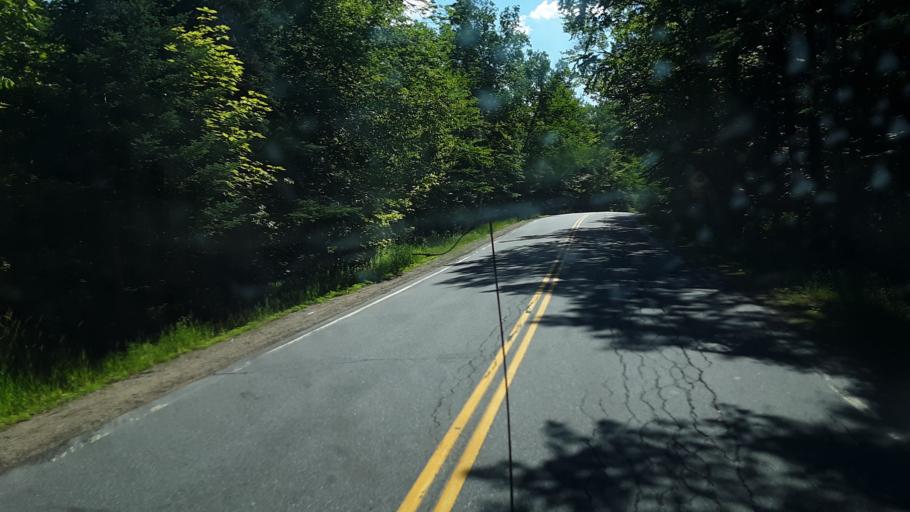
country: US
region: New Hampshire
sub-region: Grafton County
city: North Haverhill
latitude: 44.0983
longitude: -71.8694
